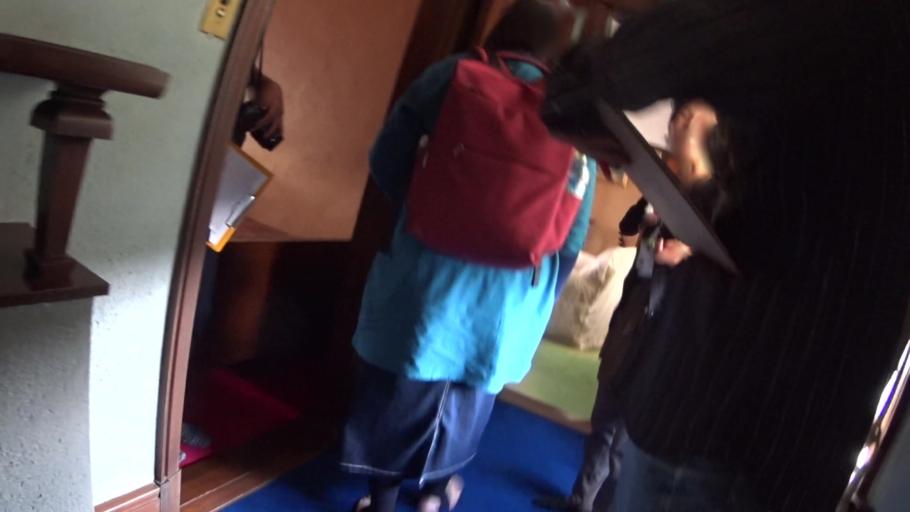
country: JP
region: Kyoto
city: Miyazu
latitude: 35.5040
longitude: 135.0921
